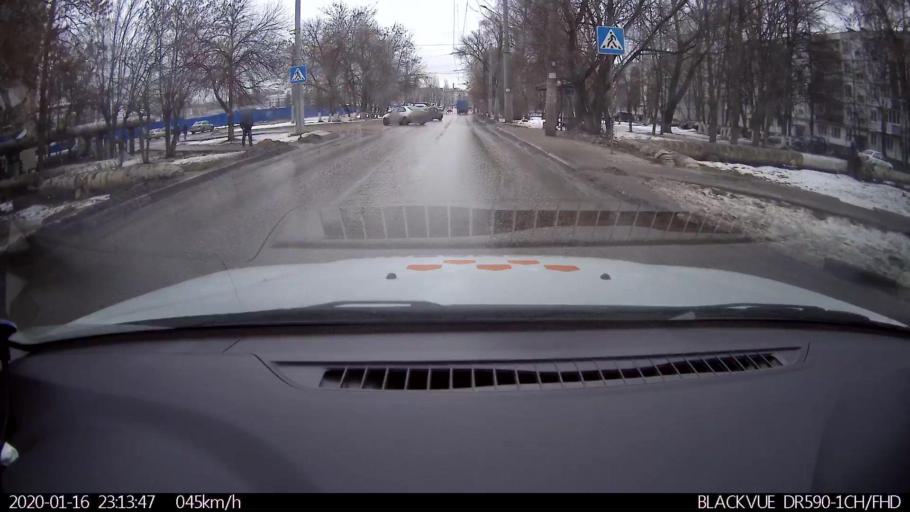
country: RU
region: Nizjnij Novgorod
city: Nizhniy Novgorod
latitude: 56.2850
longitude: 43.9220
